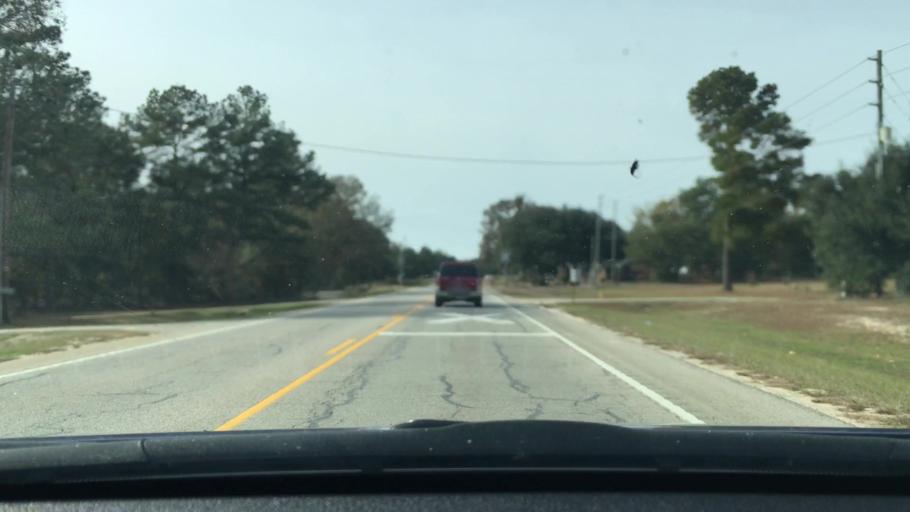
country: US
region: South Carolina
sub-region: Sumter County
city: Cherryvale
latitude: 33.9376
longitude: -80.4687
